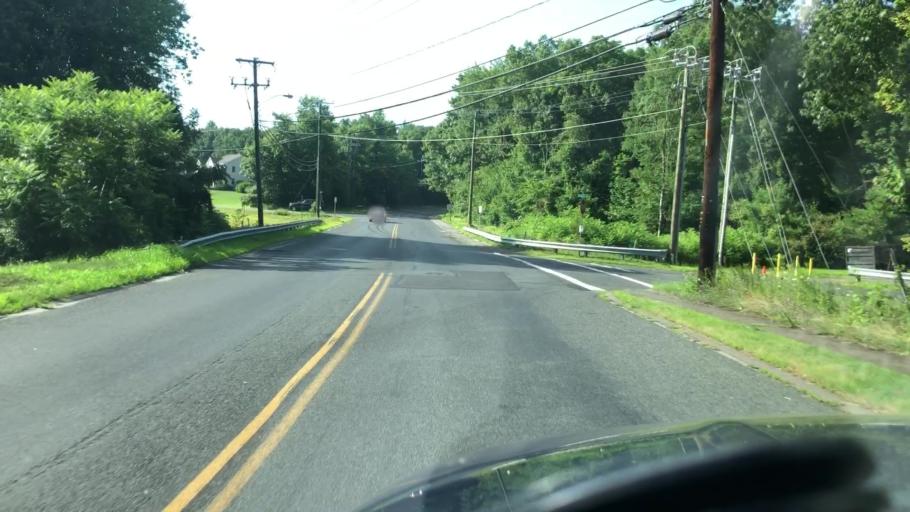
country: US
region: Massachusetts
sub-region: Hampshire County
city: Easthampton
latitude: 42.2353
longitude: -72.6863
